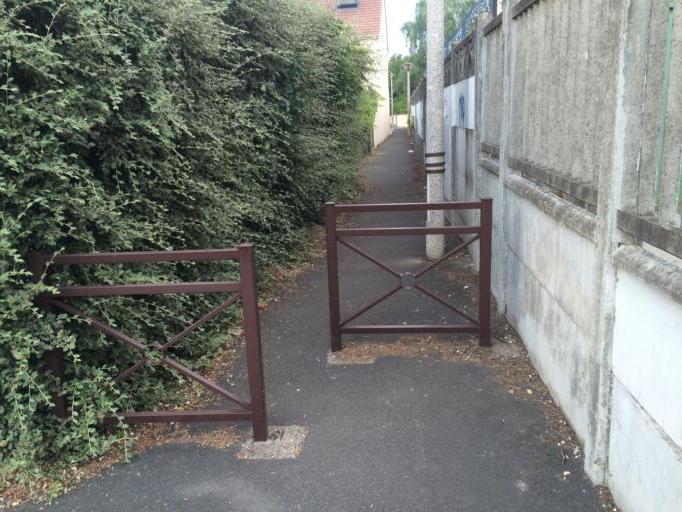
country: FR
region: Ile-de-France
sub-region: Departement de l'Essonne
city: Morsang-sur-Orge
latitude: 48.6623
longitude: 2.3536
